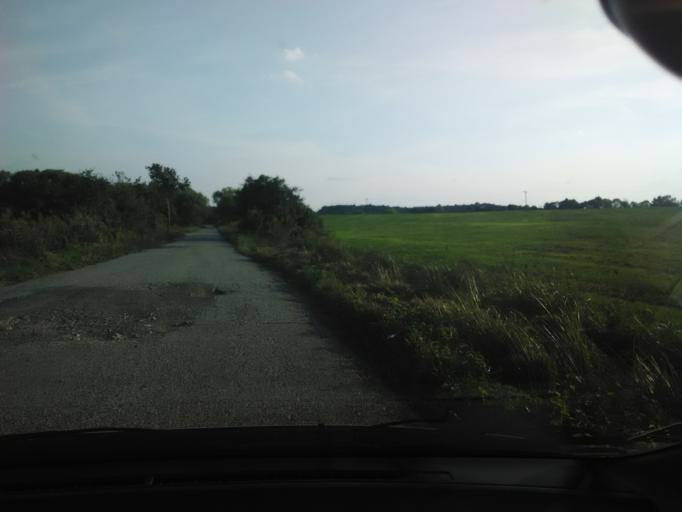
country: SK
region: Nitriansky
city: Levice
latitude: 48.3020
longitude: 18.6997
